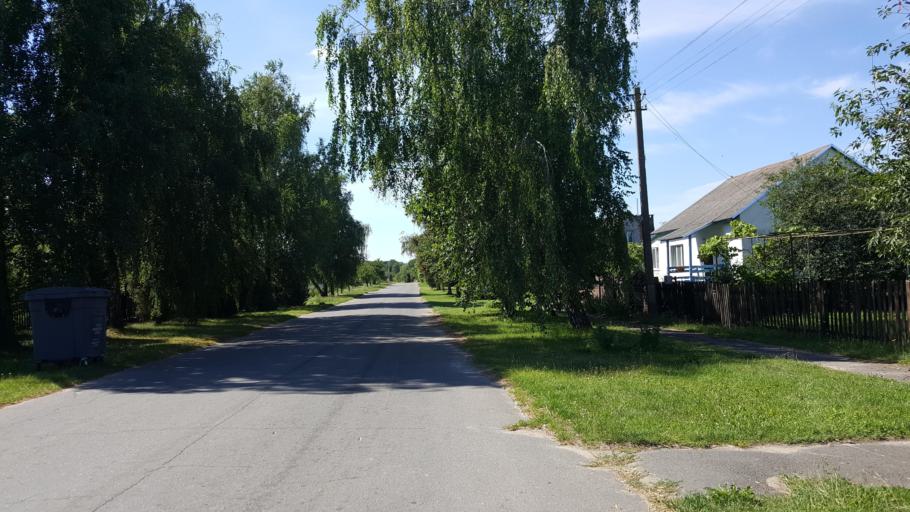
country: BY
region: Brest
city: Charnawchytsy
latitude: 52.2759
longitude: 23.7646
